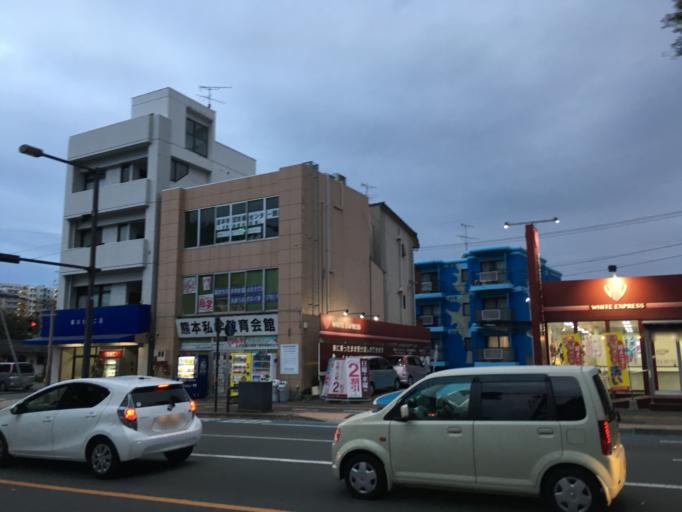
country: JP
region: Kumamoto
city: Kumamoto
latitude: 32.8016
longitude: 130.7272
